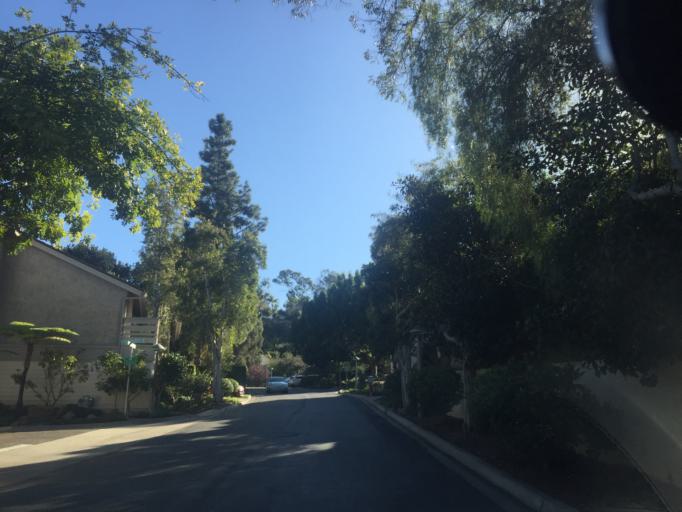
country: US
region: California
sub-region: San Diego County
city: Lemon Grove
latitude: 32.7754
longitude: -117.1008
